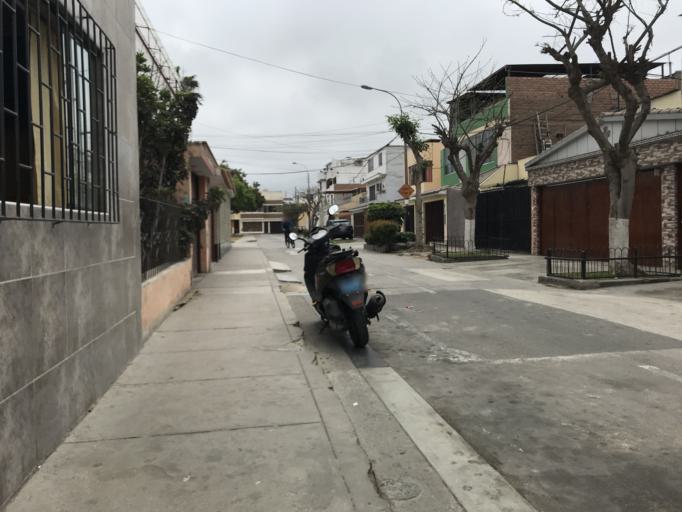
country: PE
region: Lima
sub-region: Lima
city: San Isidro
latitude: -12.0781
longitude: -77.0749
